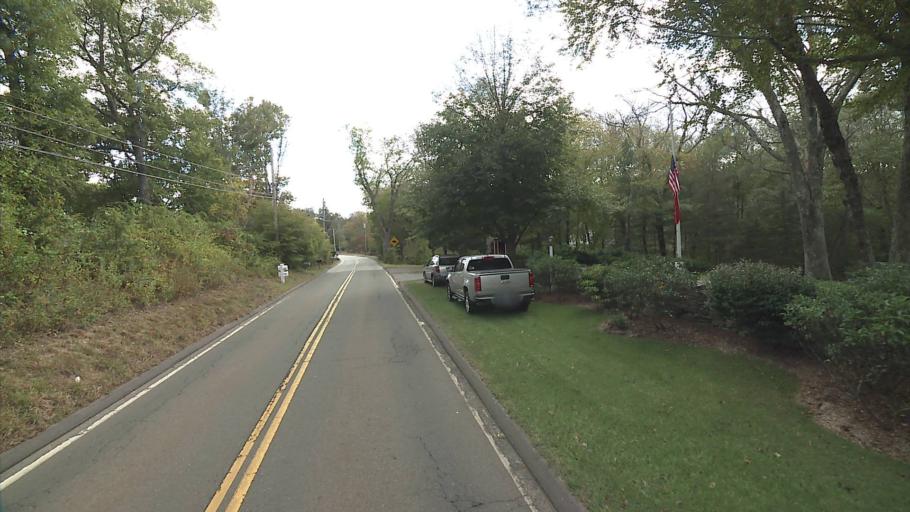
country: US
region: Connecticut
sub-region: Middlesex County
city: Durham
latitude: 41.4137
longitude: -72.6149
